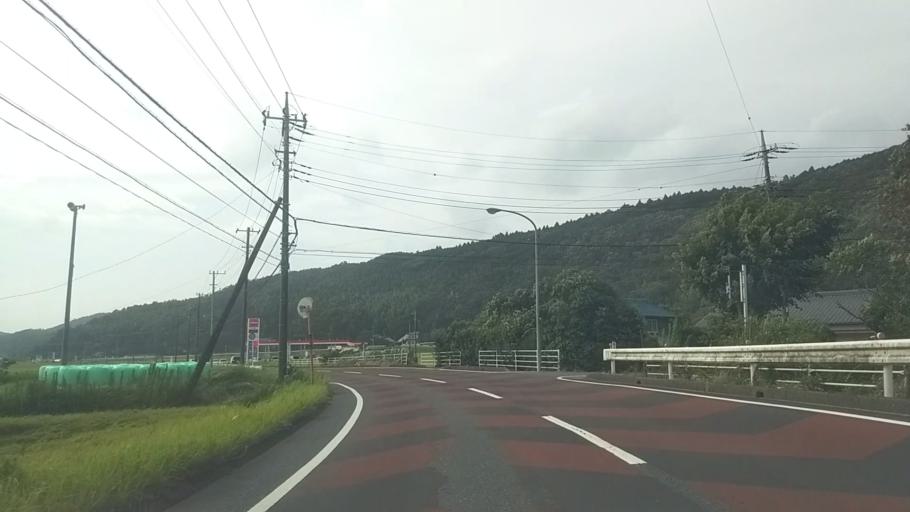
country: JP
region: Chiba
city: Kisarazu
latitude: 35.3080
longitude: 139.9765
